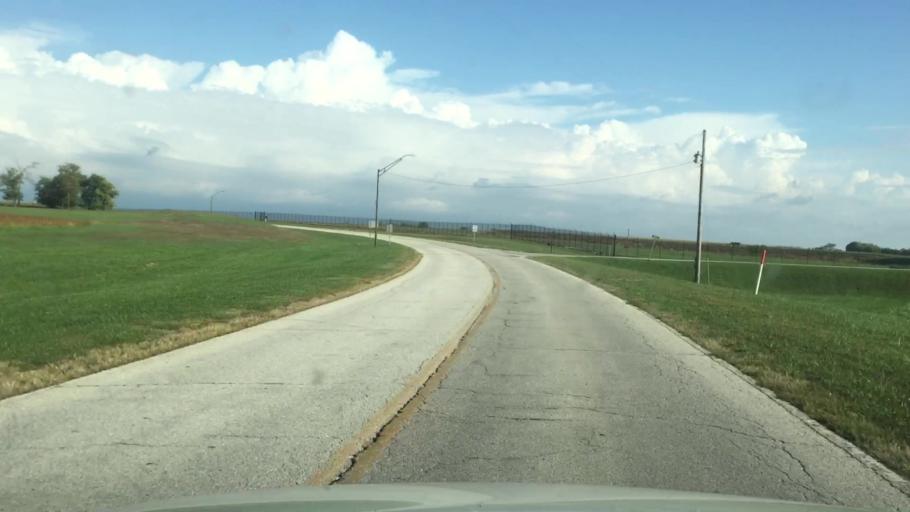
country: US
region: Missouri
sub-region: Boone County
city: Ashland
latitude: 38.8210
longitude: -92.2216
